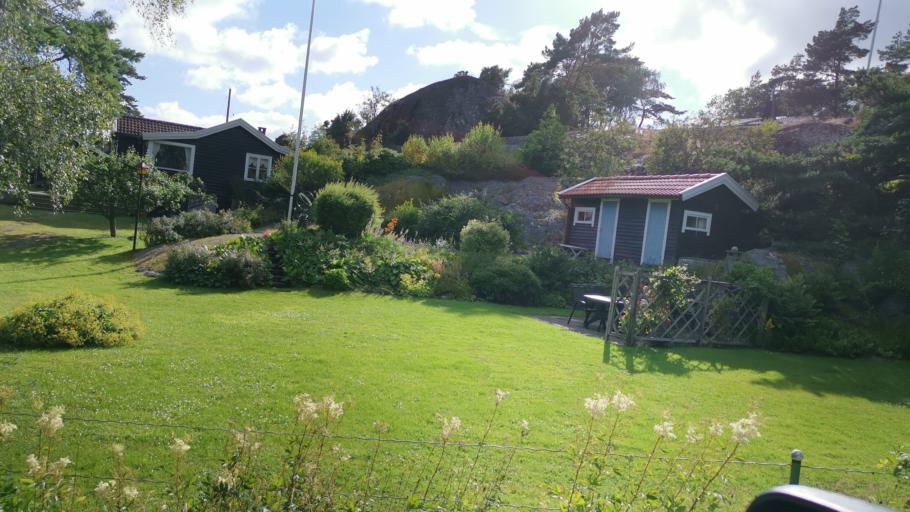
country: SE
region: Vaestra Goetaland
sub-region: Tjorns Kommun
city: Myggenas
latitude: 58.1098
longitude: 11.6541
